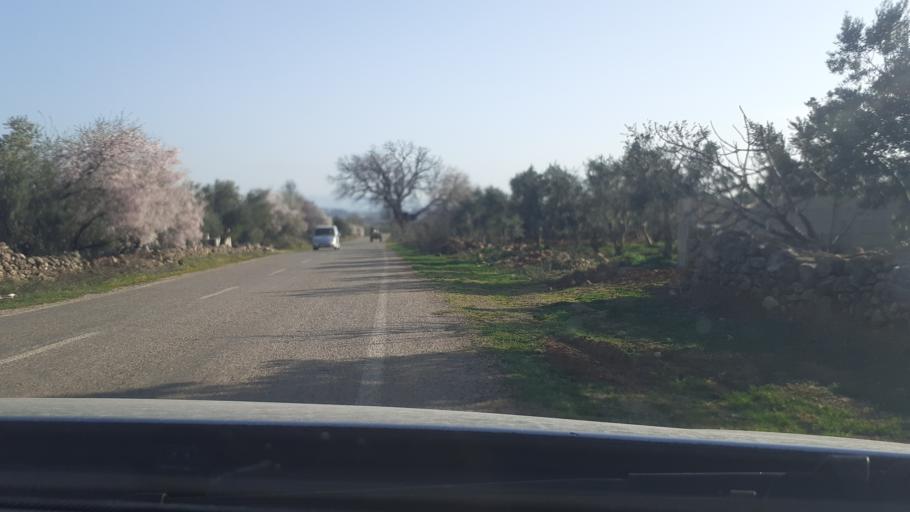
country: TR
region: Hatay
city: Aktepe
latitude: 36.7241
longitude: 36.4851
